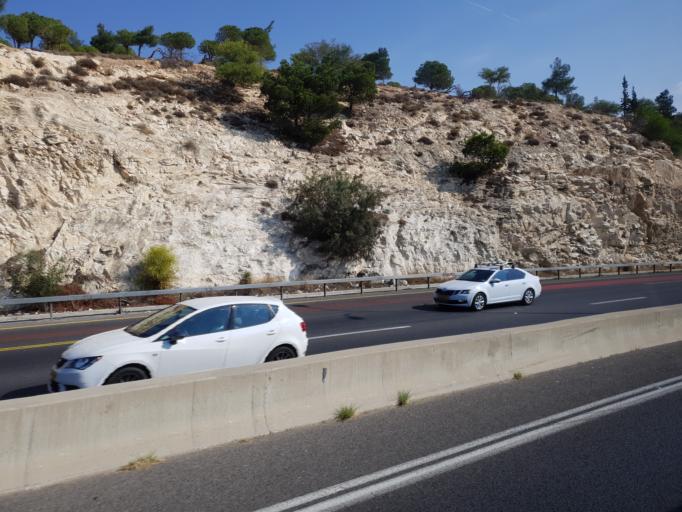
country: PS
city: Az Za`ayyim
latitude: 31.7885
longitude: 35.2779
